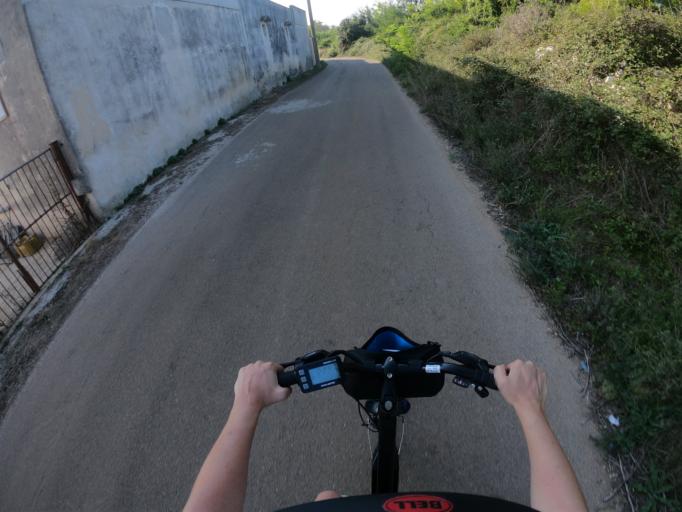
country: IT
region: Apulia
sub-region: Provincia di Lecce
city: Leuca
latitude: 39.8161
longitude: 18.3613
